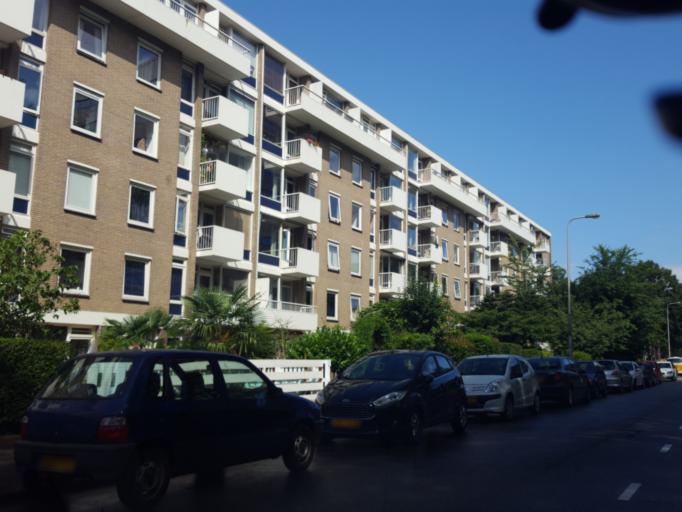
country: NL
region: Utrecht
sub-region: Gemeente Utrecht
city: Utrecht
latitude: 52.0832
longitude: 5.0918
